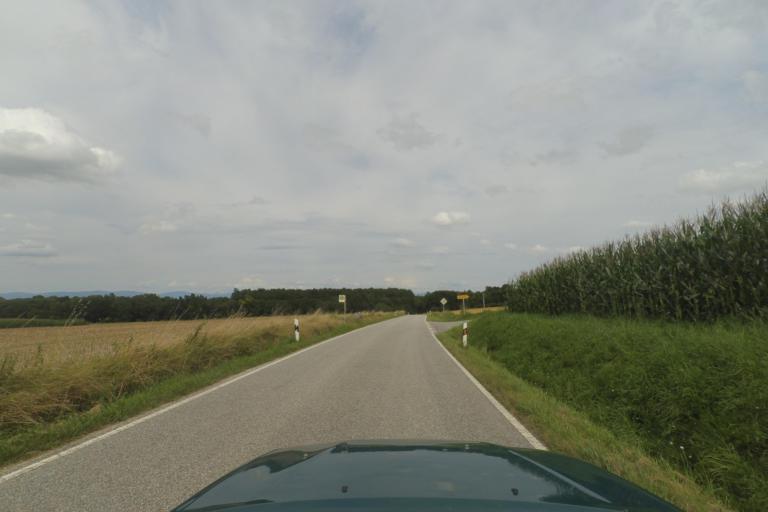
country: DE
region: Bavaria
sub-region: Lower Bavaria
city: Oberporing
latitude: 48.6872
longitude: 12.7803
